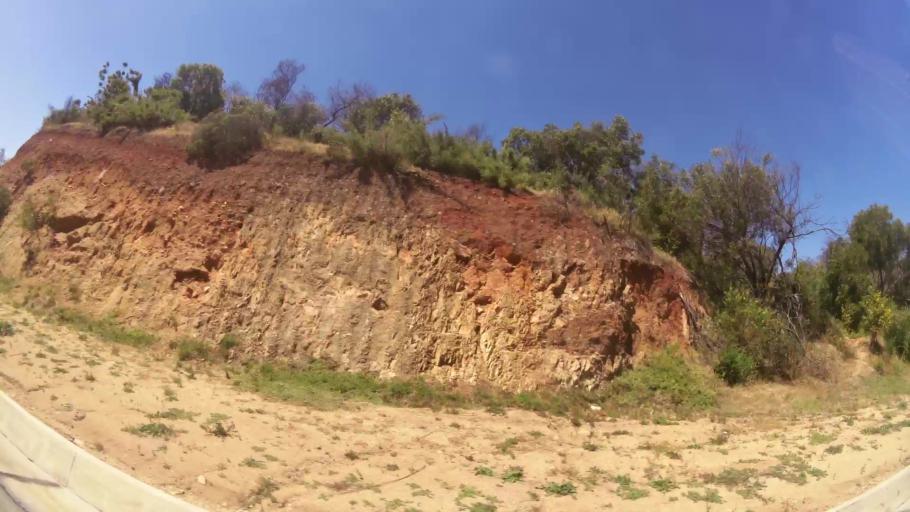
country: CL
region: Valparaiso
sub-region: Provincia de Valparaiso
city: Valparaiso
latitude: -33.0591
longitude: -71.6544
